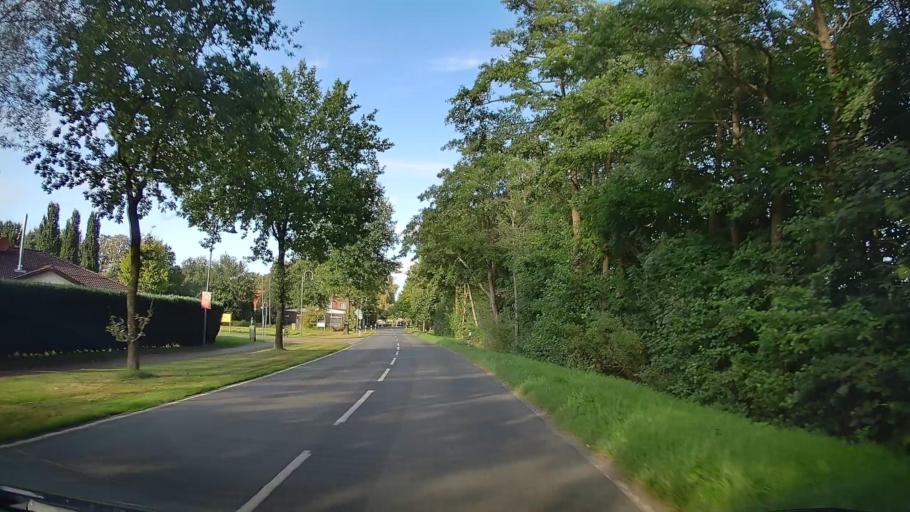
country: DE
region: Lower Saxony
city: Ostrhauderfehn
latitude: 53.1279
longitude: 7.6767
